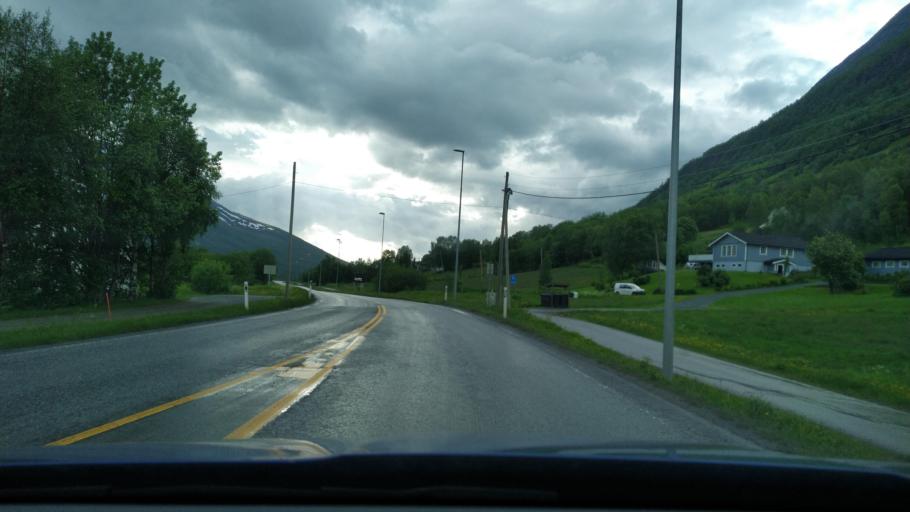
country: NO
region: Troms
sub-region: Balsfjord
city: Storsteinnes
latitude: 69.2201
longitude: 19.5521
